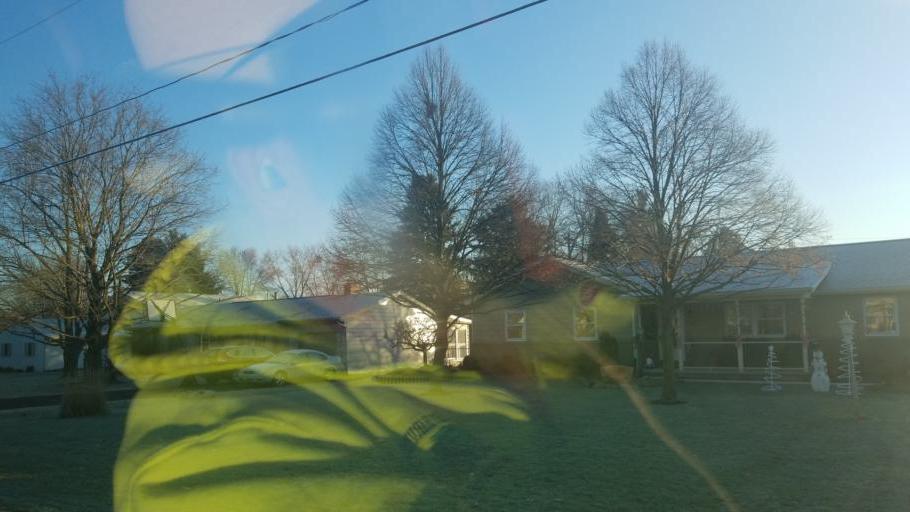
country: US
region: Ohio
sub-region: Marion County
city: Marion
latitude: 40.5774
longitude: -83.1038
